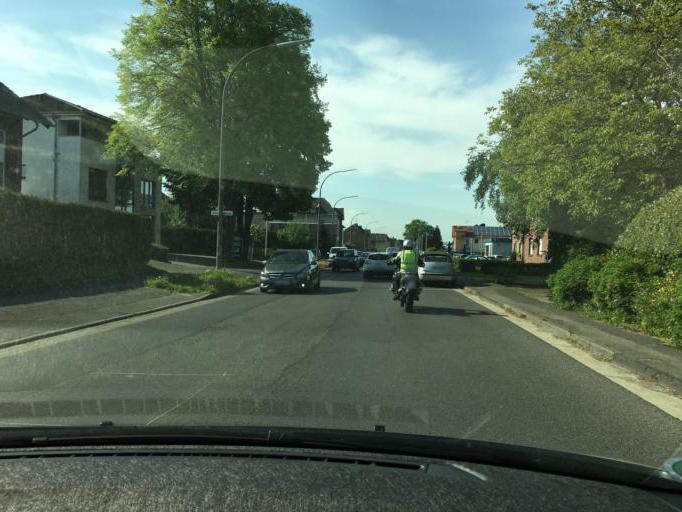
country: DE
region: North Rhine-Westphalia
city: Bruhl
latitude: 50.7789
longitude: 6.9279
